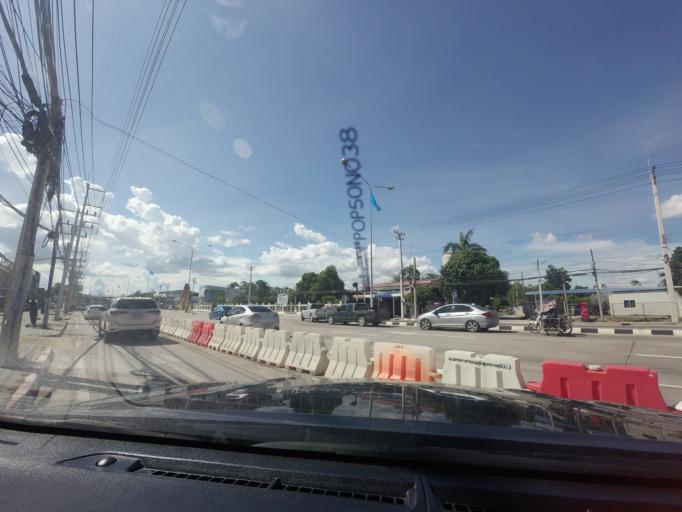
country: TH
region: Suphan Buri
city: Song Phi Nong
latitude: 14.1803
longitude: 99.9391
